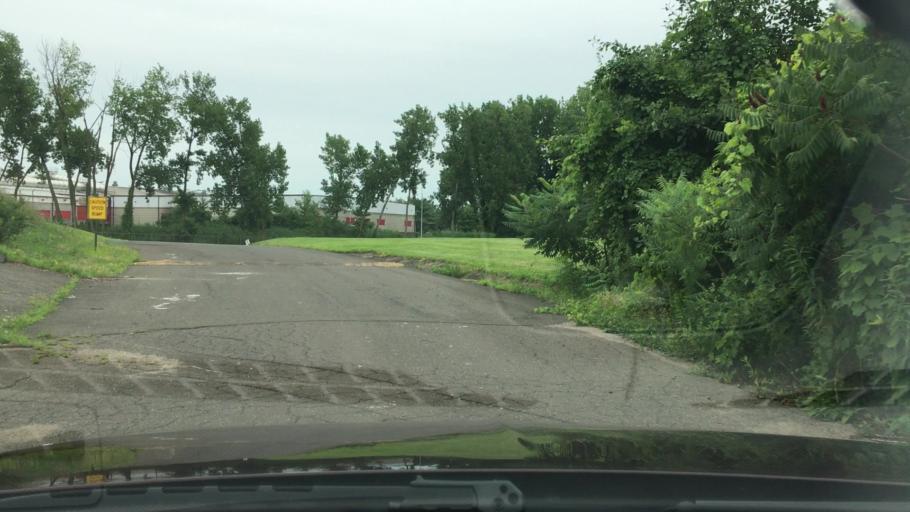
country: US
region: Connecticut
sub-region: Hartford County
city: Wethersfield
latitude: 41.7481
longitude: -72.6535
